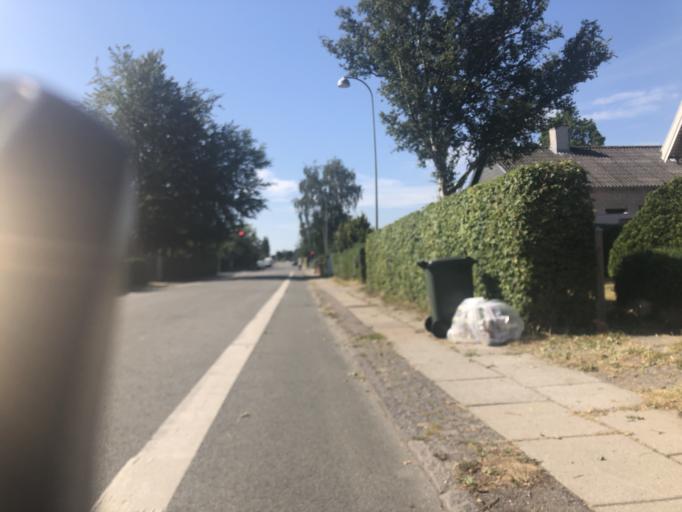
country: DK
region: Capital Region
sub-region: Gladsaxe Municipality
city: Buddinge
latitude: 55.7459
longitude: 12.4780
